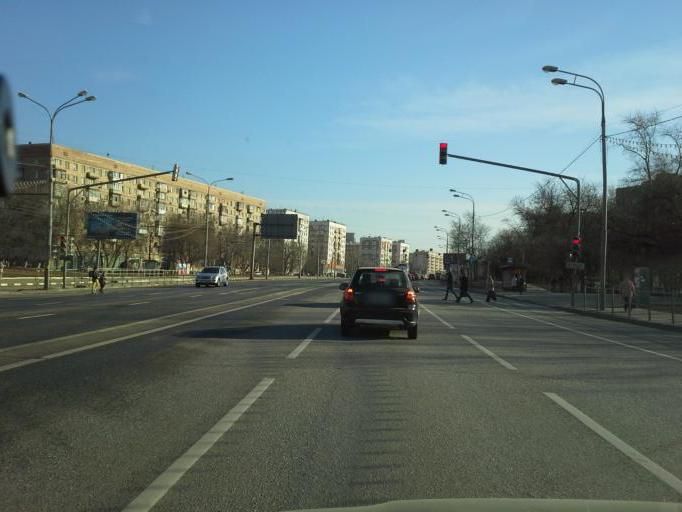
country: RU
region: Moscow
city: Taganskiy
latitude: 55.7275
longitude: 37.6627
